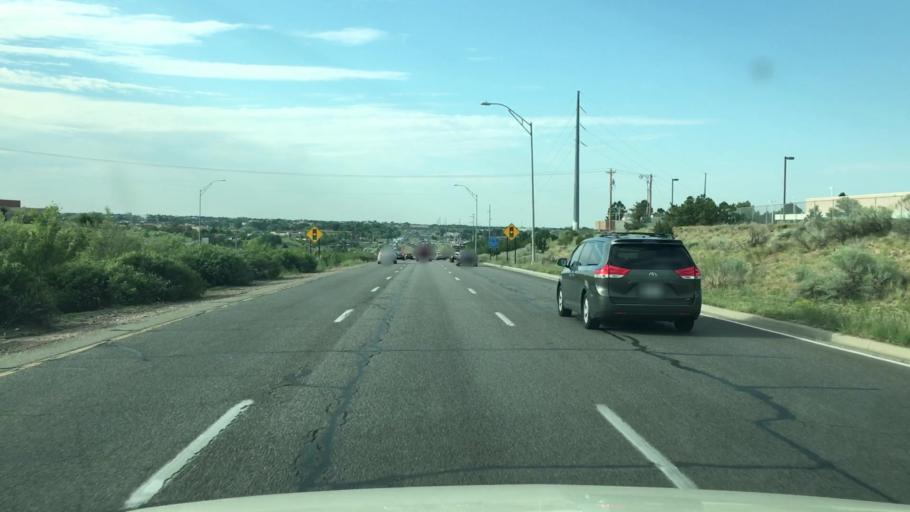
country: US
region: New Mexico
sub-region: Santa Fe County
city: Santa Fe
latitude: 35.6552
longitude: -105.9568
